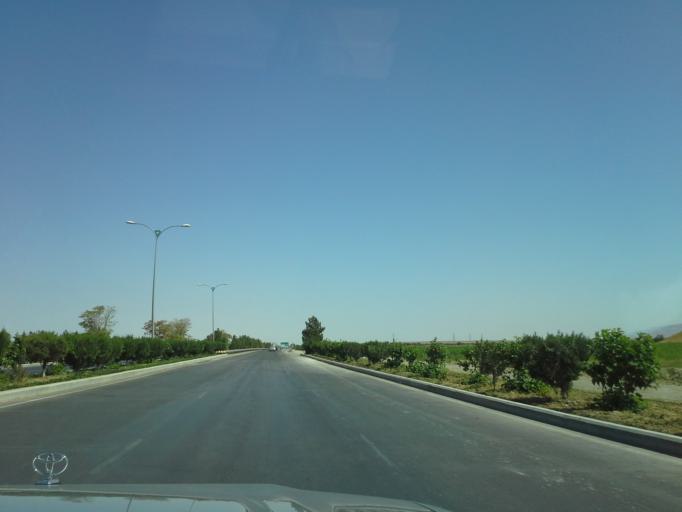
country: TM
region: Ahal
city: Annau
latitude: 37.9061
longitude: 58.5283
